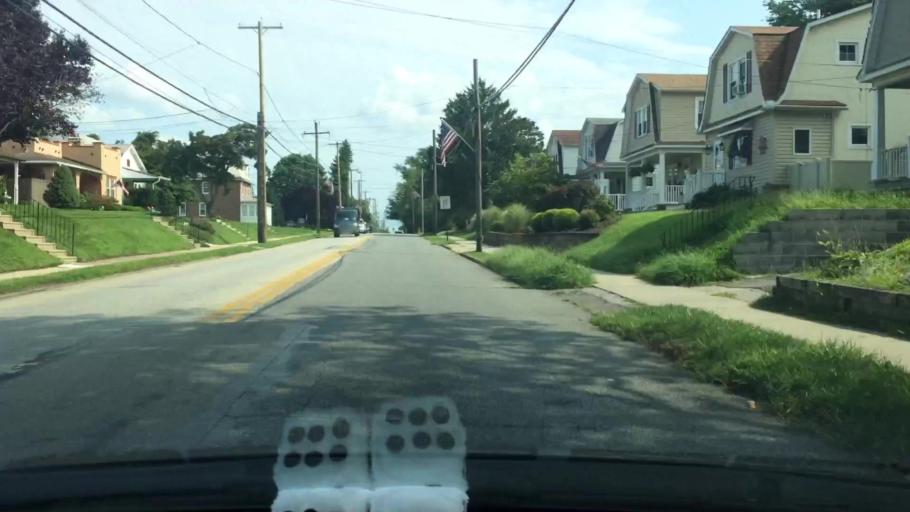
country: US
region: Pennsylvania
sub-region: Delaware County
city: Prospect Park
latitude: 39.8914
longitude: -75.3128
